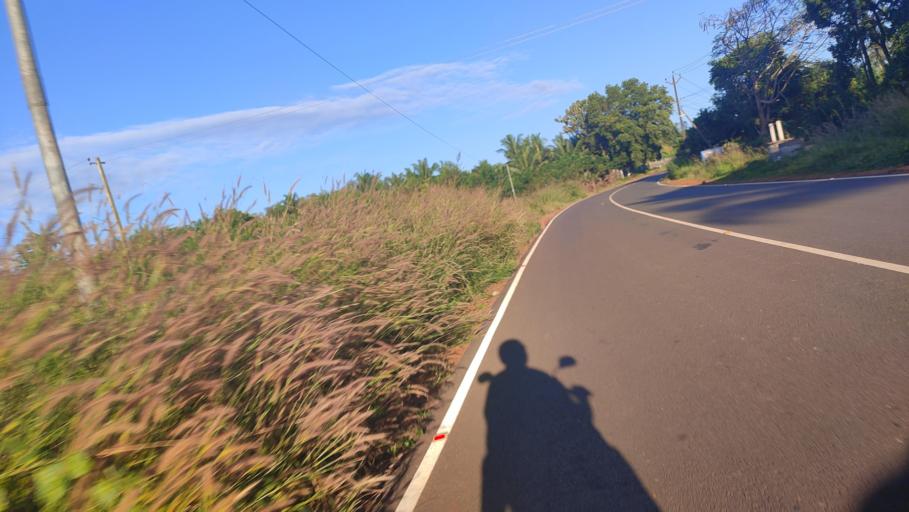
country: IN
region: Kerala
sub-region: Kasaragod District
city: Kasaragod
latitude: 12.4656
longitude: 75.0627
